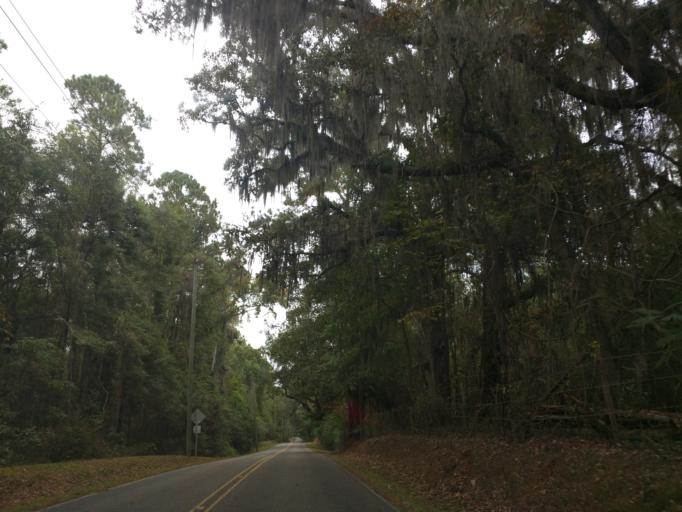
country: US
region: Florida
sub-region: Leon County
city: Tallahassee
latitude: 30.4207
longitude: -84.2101
